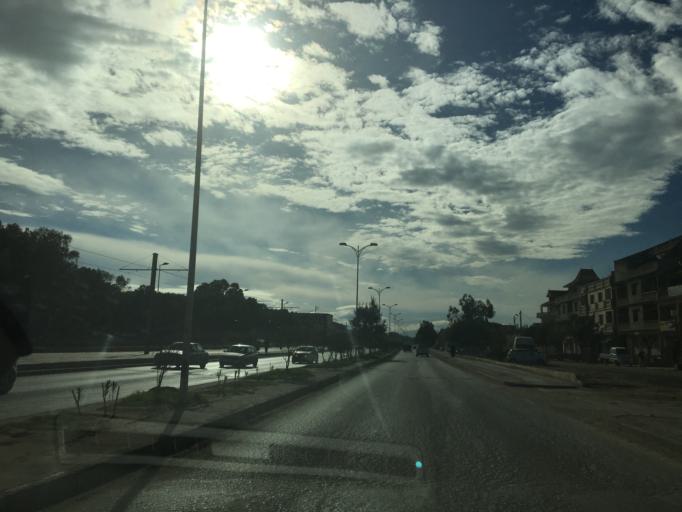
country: DZ
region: Alger
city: Ain Taya
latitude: 36.7731
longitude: 3.2448
